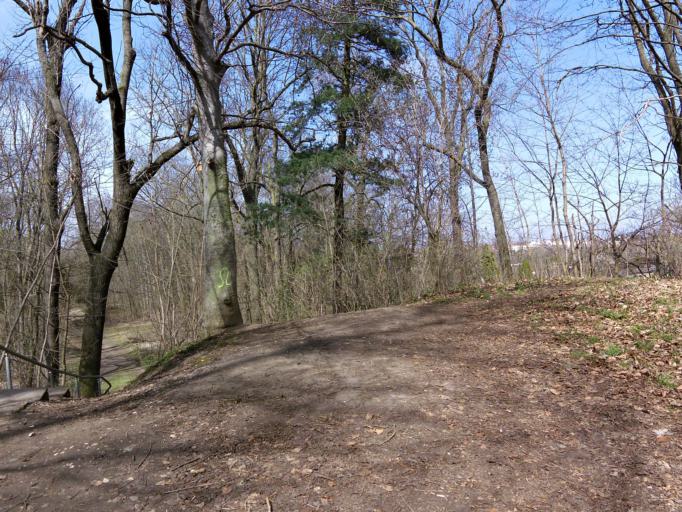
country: DE
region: Saxony
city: Leipzig
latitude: 51.3574
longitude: 12.3471
